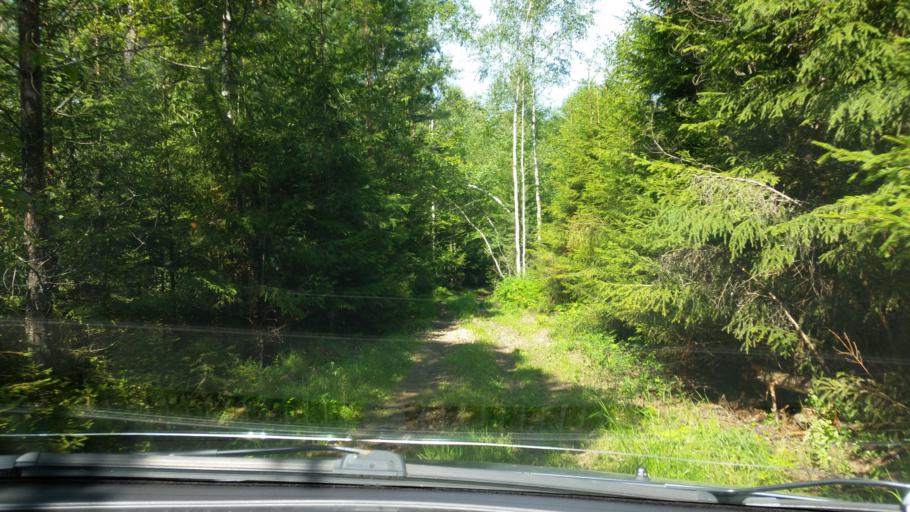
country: RU
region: Moskovskaya
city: Bol'shoye Gryzlovo
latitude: 54.9096
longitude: 37.7558
